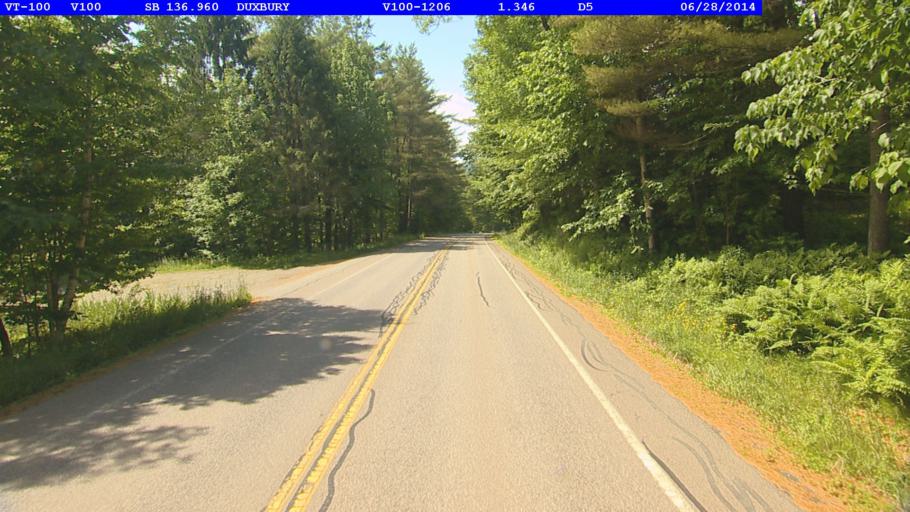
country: US
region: Vermont
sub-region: Washington County
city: Waterbury
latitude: 44.2654
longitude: -72.7854
